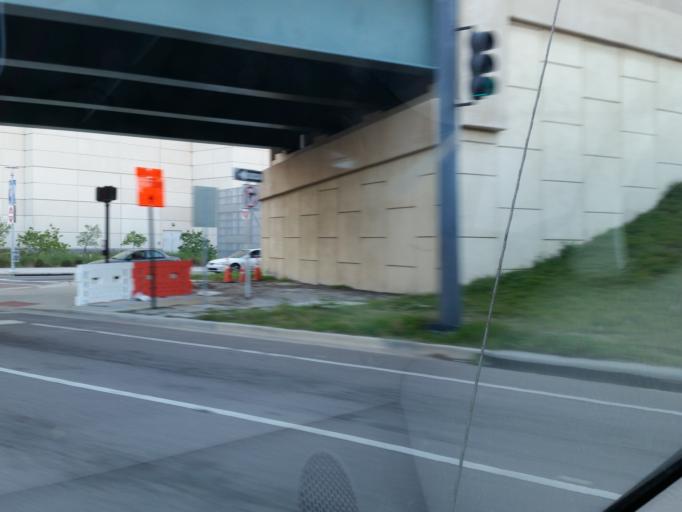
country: US
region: Florida
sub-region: Orange County
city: Orlando
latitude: 28.5384
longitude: -81.3827
